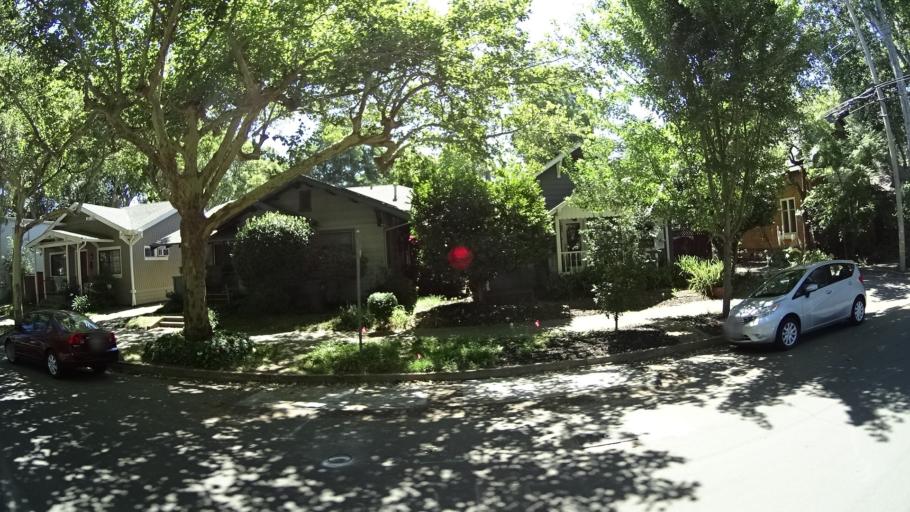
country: US
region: California
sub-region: Sacramento County
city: Sacramento
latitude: 38.5826
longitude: -121.4714
